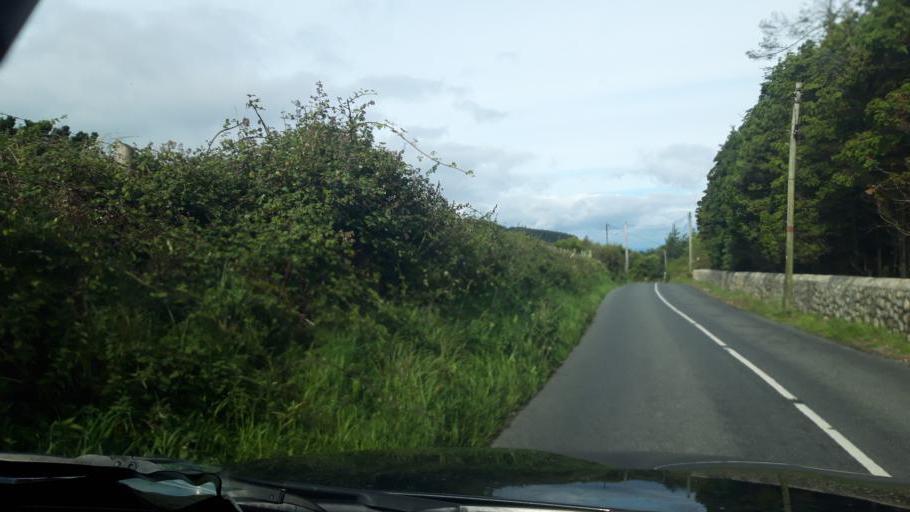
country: IE
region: Leinster
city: Sandyford
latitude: 53.2305
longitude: -6.2209
